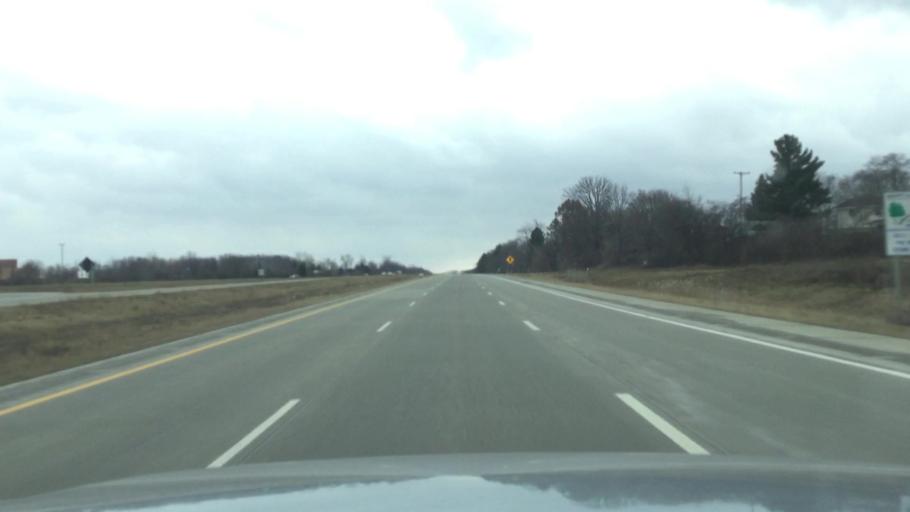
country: US
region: Michigan
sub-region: Genesee County
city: Grand Blanc
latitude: 42.9437
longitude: -83.6818
